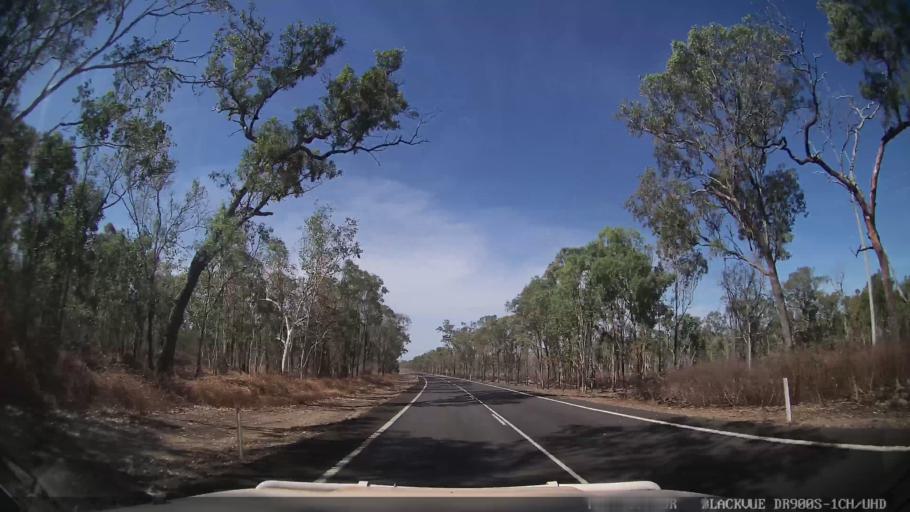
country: AU
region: Queensland
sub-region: Cook
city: Cooktown
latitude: -15.7875
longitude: 144.9520
